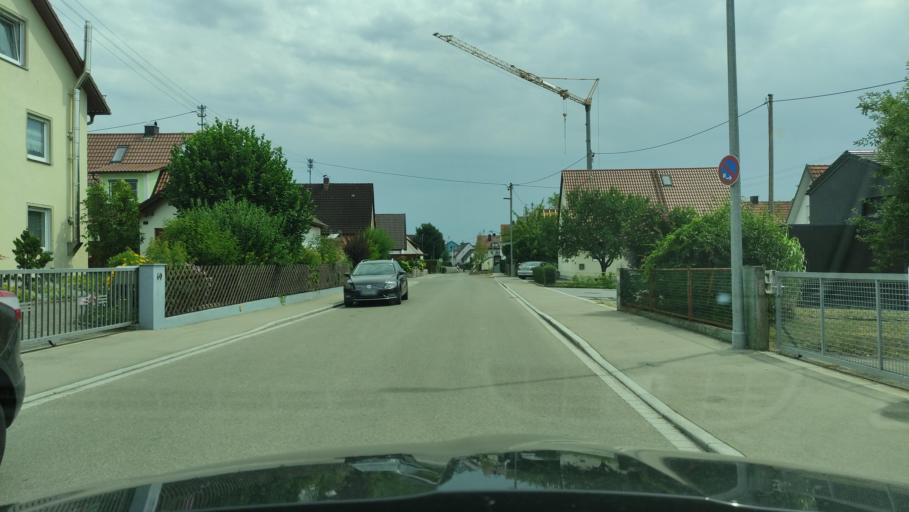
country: DE
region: Bavaria
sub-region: Swabia
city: Krumbach
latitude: 48.2503
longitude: 10.3653
